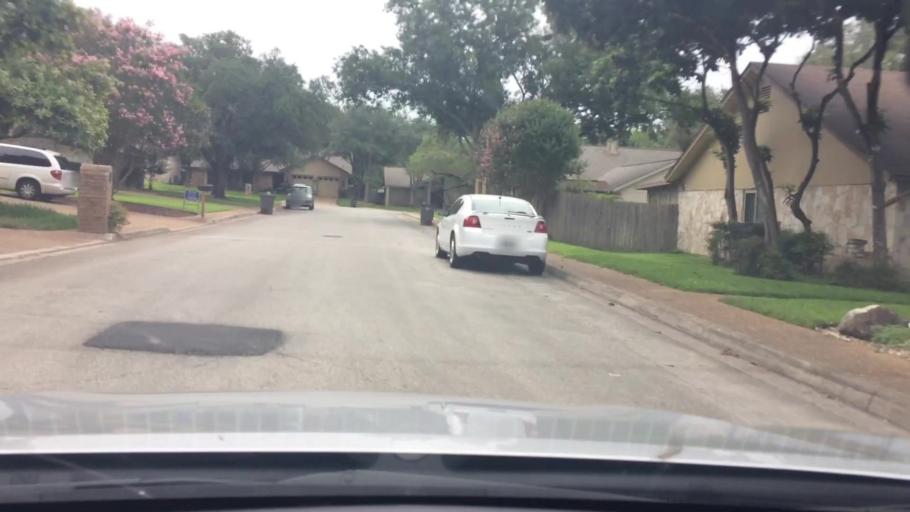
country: US
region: Texas
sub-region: Bexar County
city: Hollywood Park
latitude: 29.5790
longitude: -98.4575
